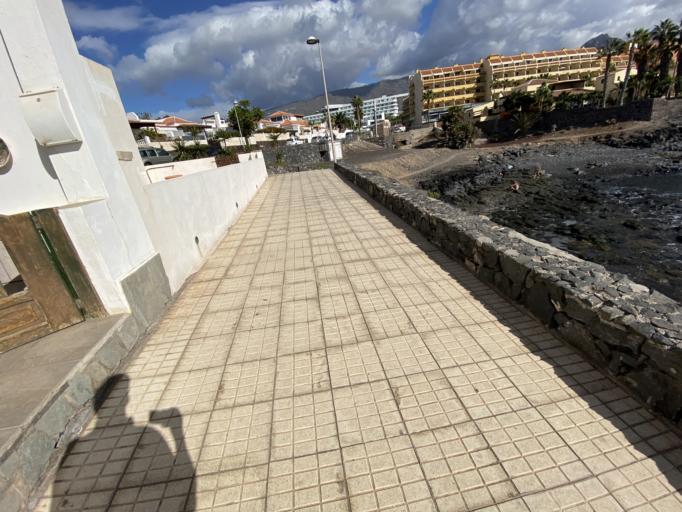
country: ES
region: Canary Islands
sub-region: Provincia de Santa Cruz de Tenerife
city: Adeje
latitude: 28.0988
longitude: -16.7552
